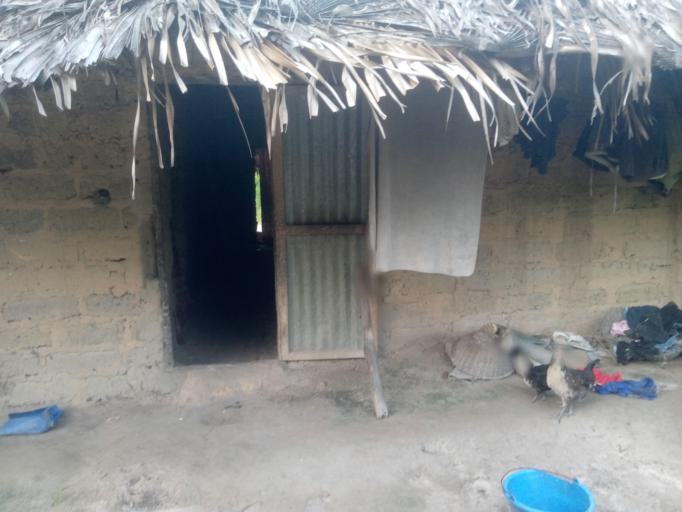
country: GM
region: Western
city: Gunjur
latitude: 13.0359
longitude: -16.7251
